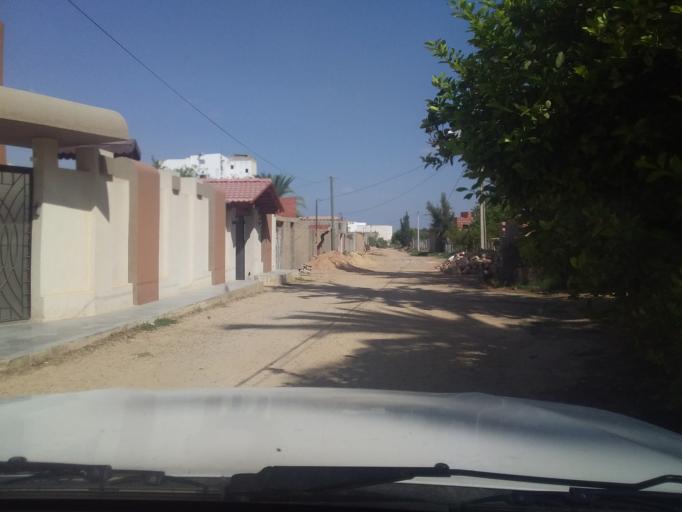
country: TN
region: Qabis
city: Gabes
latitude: 33.6259
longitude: 10.2825
